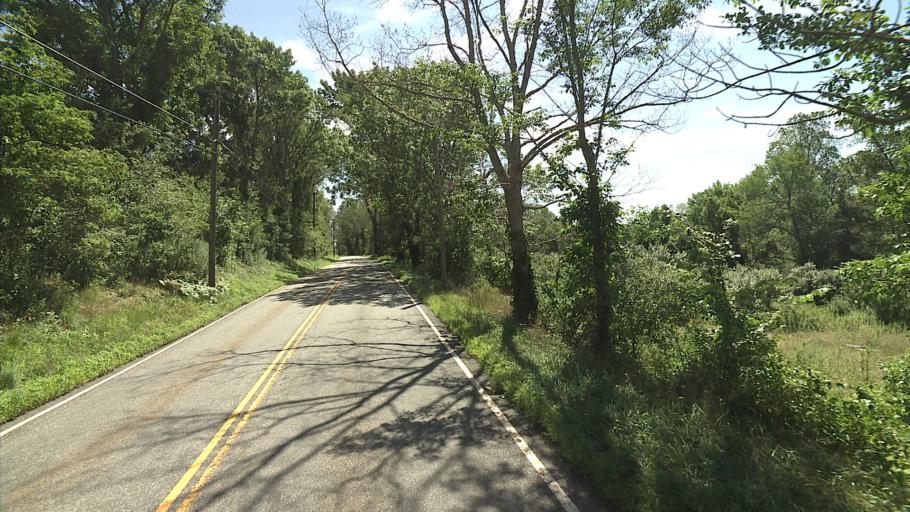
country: US
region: Connecticut
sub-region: Windham County
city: South Woodstock
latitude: 41.8654
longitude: -72.0069
